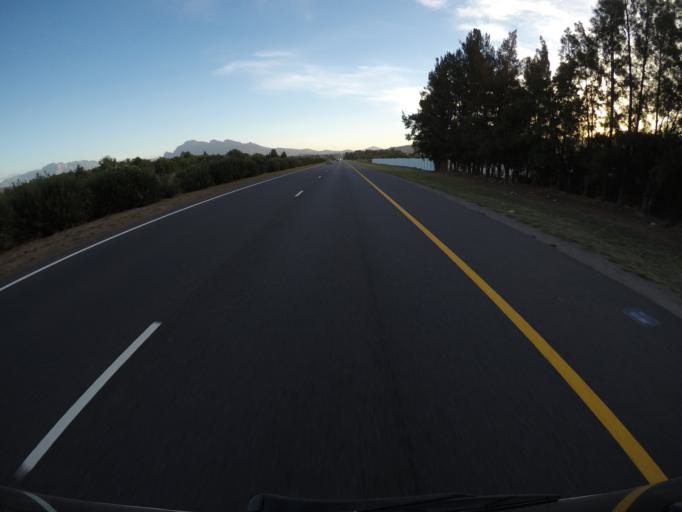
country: ZA
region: Western Cape
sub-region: Cape Winelands District Municipality
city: Paarl
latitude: -33.7518
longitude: 18.9906
